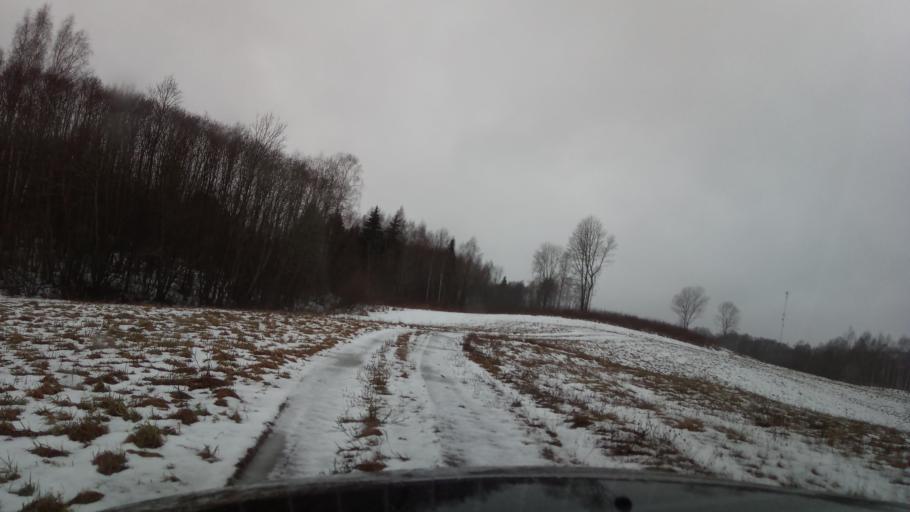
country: LT
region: Utenos apskritis
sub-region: Utena
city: Utena
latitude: 55.3642
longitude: 25.8106
